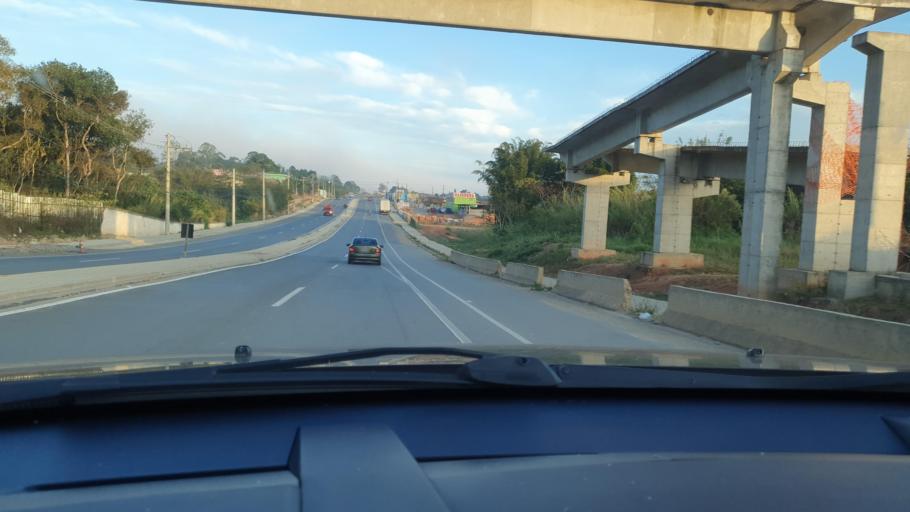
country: BR
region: Sao Paulo
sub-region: Ibiuna
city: Ibiuna
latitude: -23.6492
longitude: -47.1337
